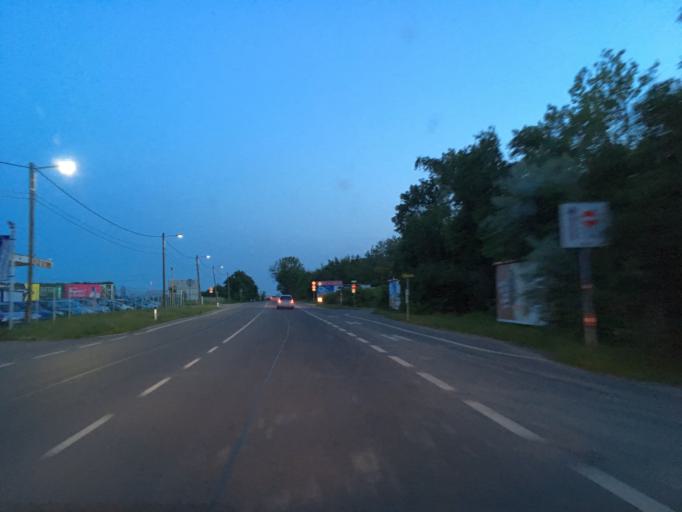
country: AT
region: Lower Austria
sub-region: Politischer Bezirk Korneuburg
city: Hagenbrunn
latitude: 48.3088
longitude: 16.4271
